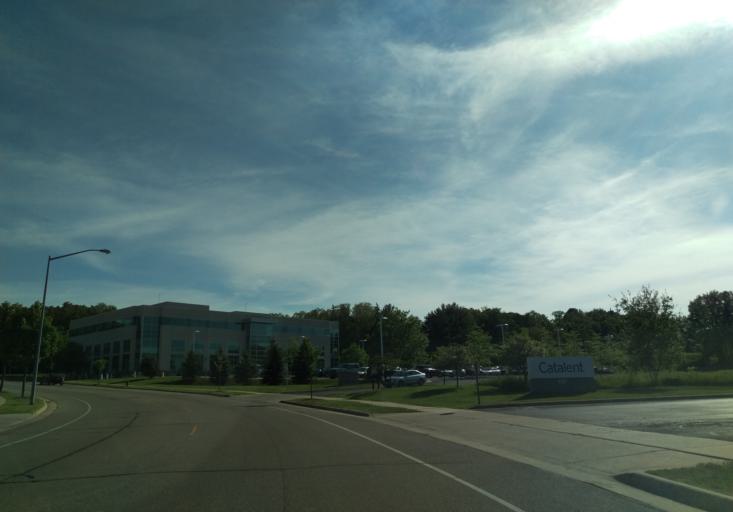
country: US
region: Wisconsin
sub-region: Dane County
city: Middleton
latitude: 43.0764
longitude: -89.5326
